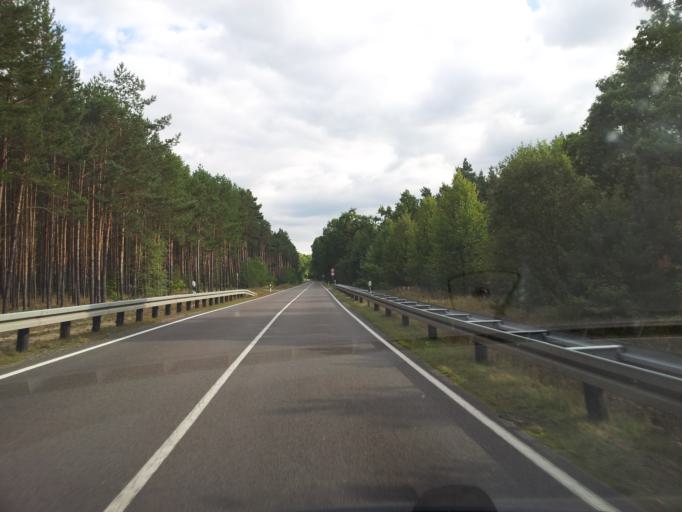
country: DE
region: Brandenburg
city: Schwarzbach
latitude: 51.4402
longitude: 13.9004
